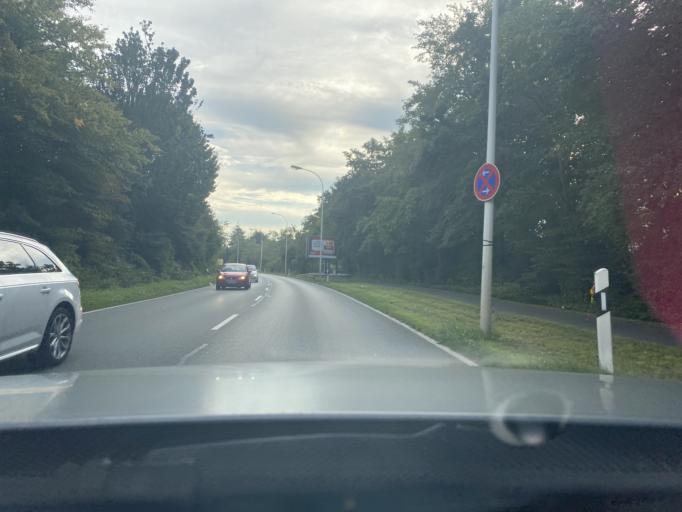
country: DE
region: Hesse
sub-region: Regierungsbezirk Darmstadt
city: Darmstadt
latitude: 49.8901
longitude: 8.6568
